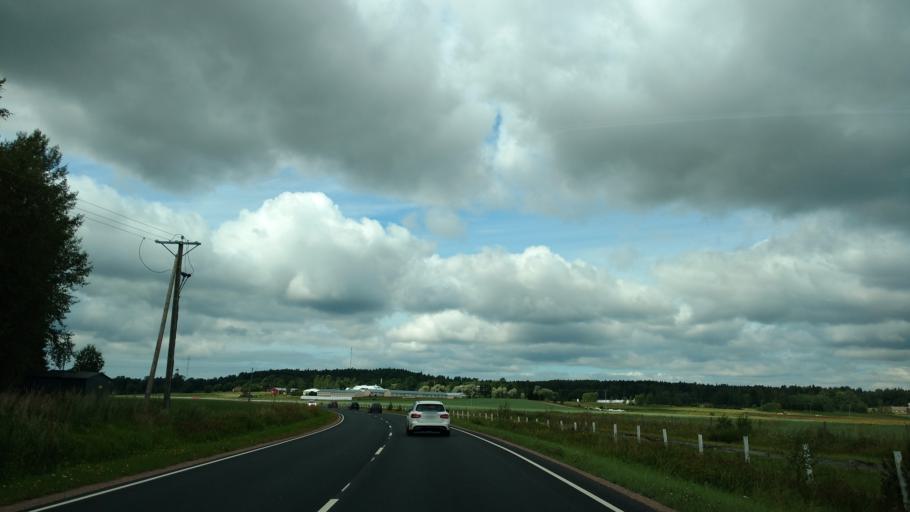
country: FI
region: Varsinais-Suomi
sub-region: Aboland-Turunmaa
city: Kimito
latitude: 60.1702
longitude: 22.7682
